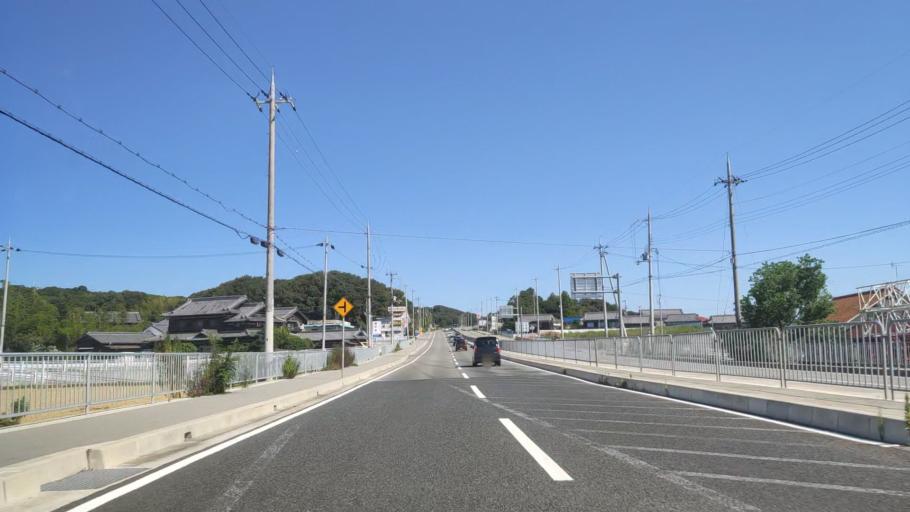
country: JP
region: Hyogo
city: Akashi
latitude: 34.7157
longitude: 134.9836
